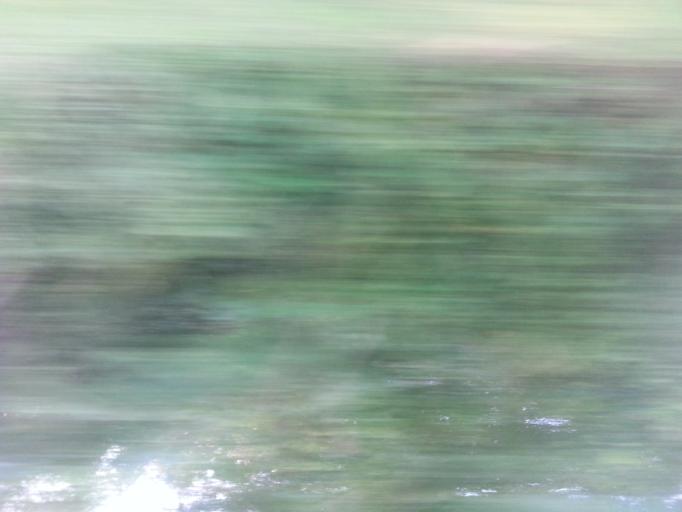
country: US
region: Tennessee
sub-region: Sevier County
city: Seymour
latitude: 35.9068
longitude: -83.8274
